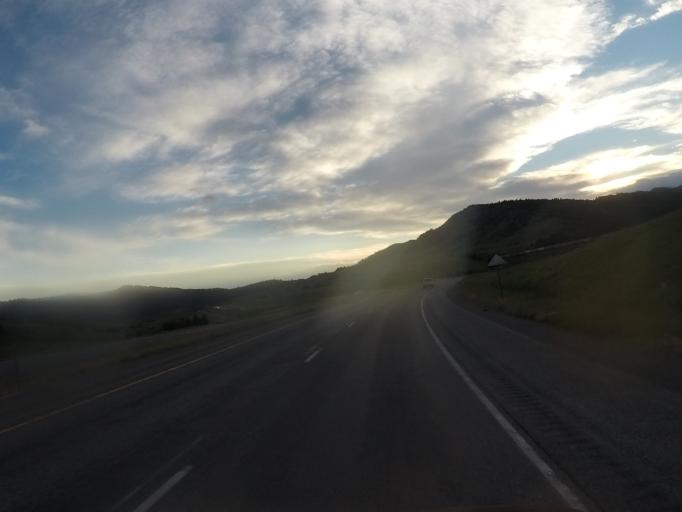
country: US
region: Montana
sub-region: Park County
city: Livingston
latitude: 45.6614
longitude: -110.7341
